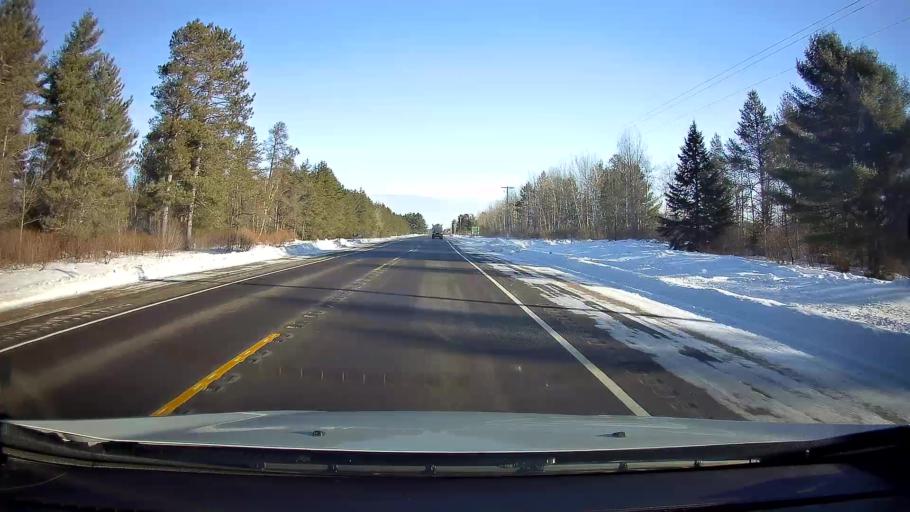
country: US
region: Wisconsin
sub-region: Sawyer County
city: Hayward
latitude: 46.0950
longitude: -91.3859
